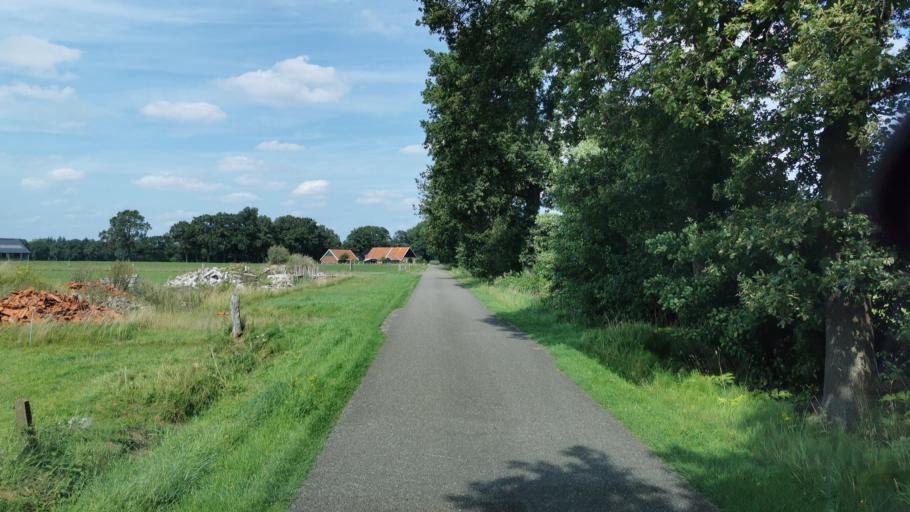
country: NL
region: Overijssel
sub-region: Gemeente Enschede
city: Enschede
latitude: 52.1657
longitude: 6.8936
